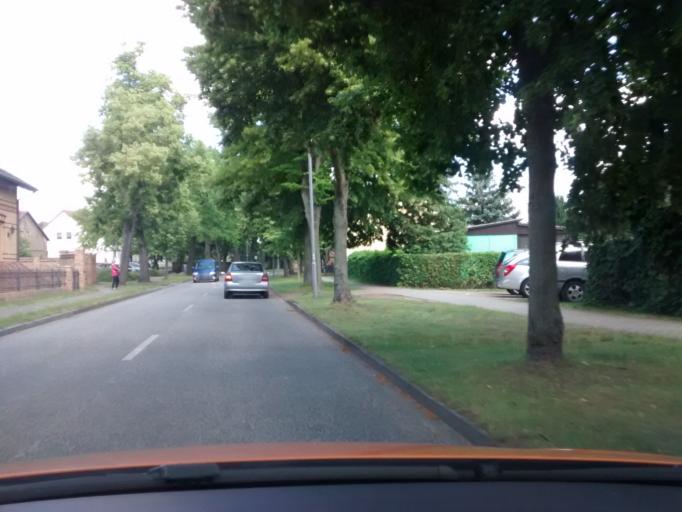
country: DE
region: Brandenburg
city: Ludwigsfelde
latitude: 52.2835
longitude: 13.2071
